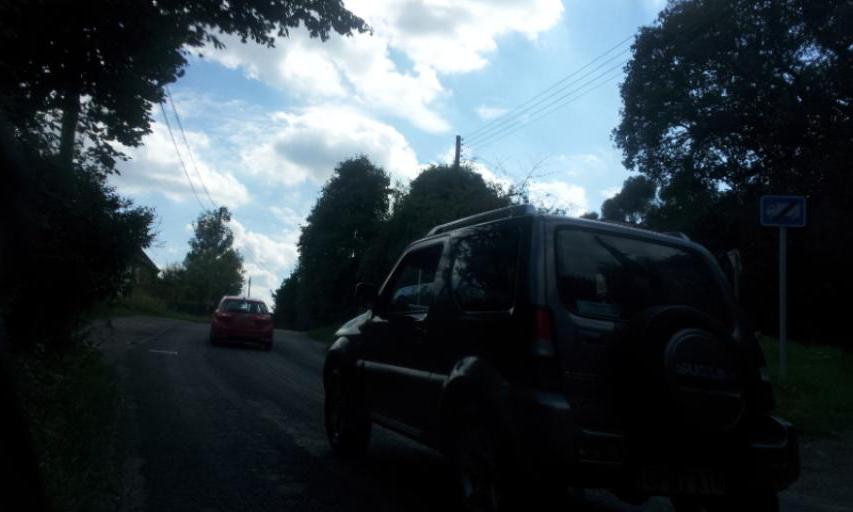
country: GB
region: England
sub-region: Kent
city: Harrietsham
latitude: 51.2014
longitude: 0.6719
